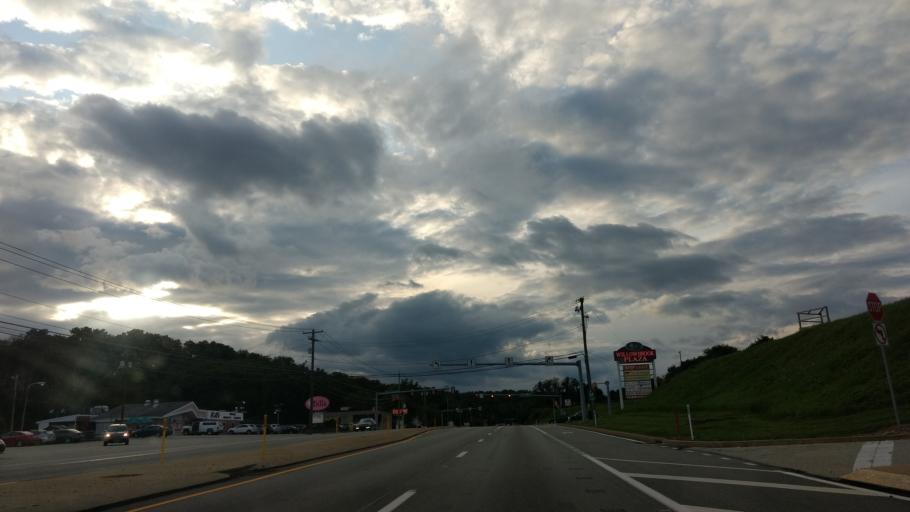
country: US
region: Pennsylvania
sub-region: Westmoreland County
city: Fellsburg
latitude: 40.1840
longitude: -79.8108
